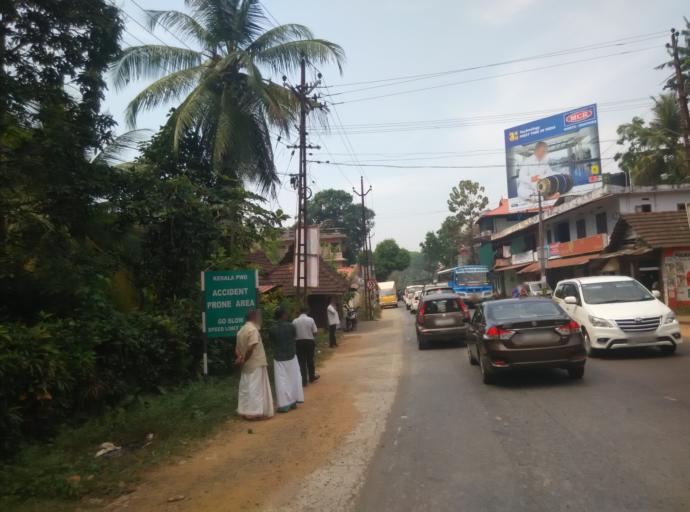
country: IN
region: Kerala
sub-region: Kottayam
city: Lalam
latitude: 9.7016
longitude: 76.6567
